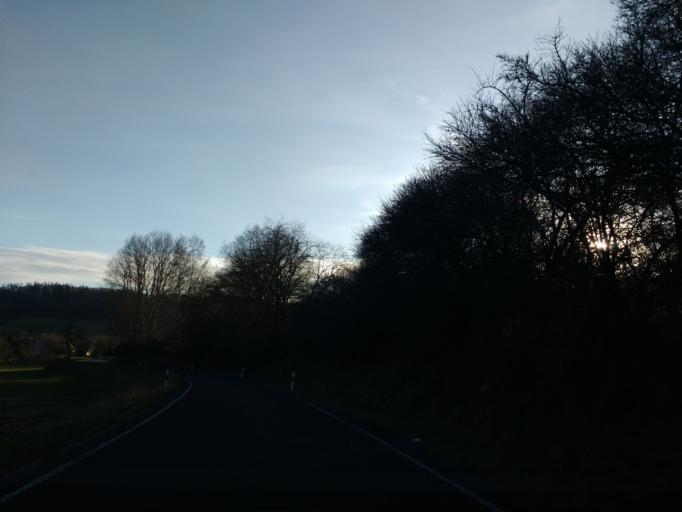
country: DE
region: Thuringia
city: Burgwalde
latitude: 51.3767
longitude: 10.0411
